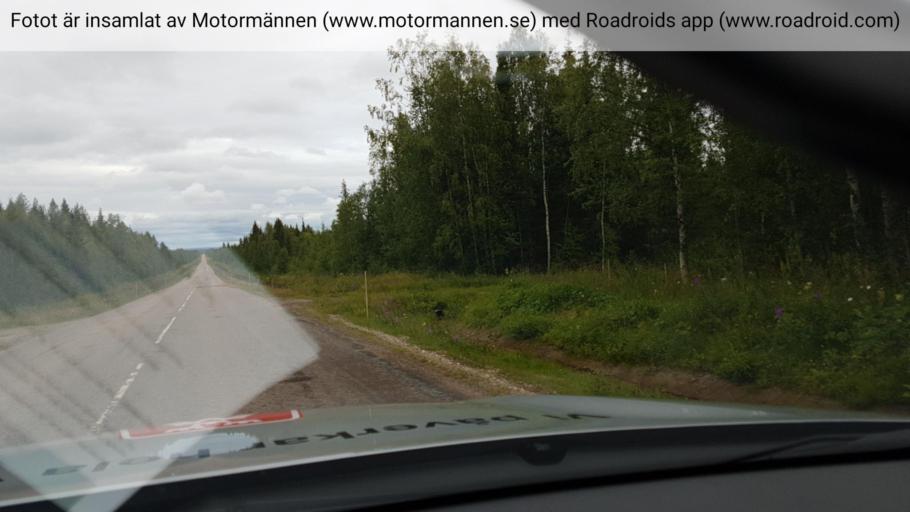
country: SE
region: Norrbotten
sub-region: Overkalix Kommun
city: OEverkalix
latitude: 67.0667
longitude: 22.4178
